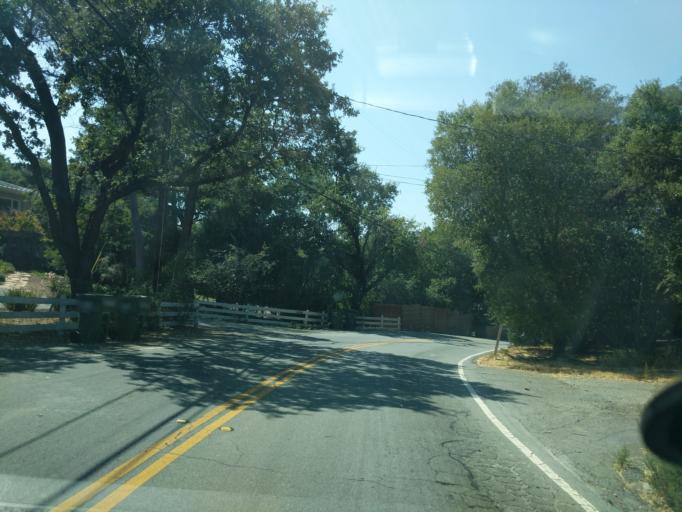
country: US
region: California
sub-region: Contra Costa County
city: Saranap
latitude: 37.8751
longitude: -122.0533
